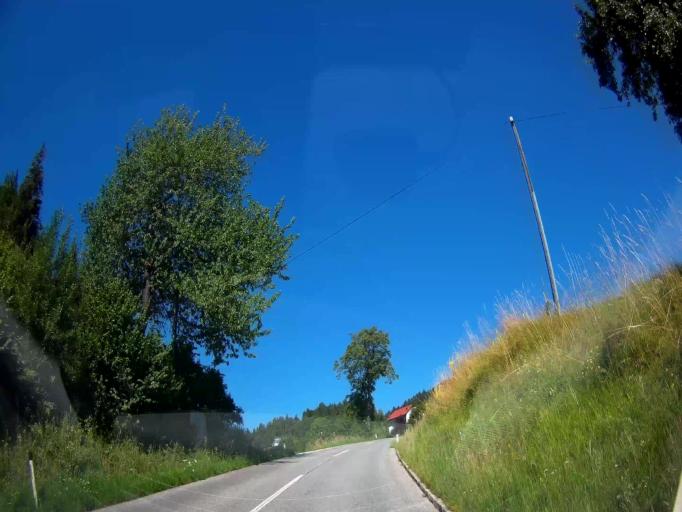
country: AT
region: Carinthia
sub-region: Politischer Bezirk Klagenfurt Land
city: Maria Worth
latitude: 46.5978
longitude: 14.1541
